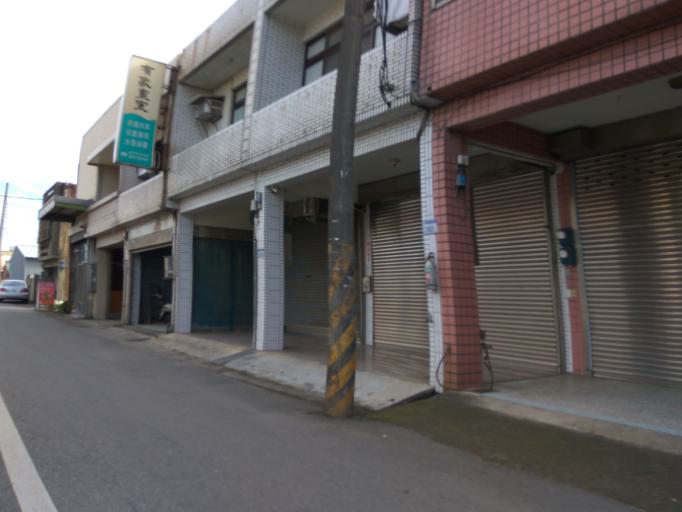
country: TW
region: Taiwan
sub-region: Hsinchu
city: Zhubei
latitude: 24.9649
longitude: 121.0972
